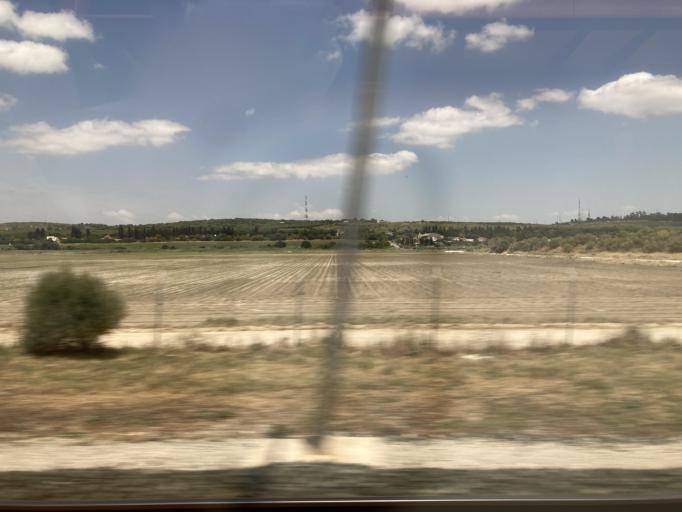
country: ES
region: Andalusia
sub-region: Provincia de Cadiz
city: El Puerto de Santa Maria
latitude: 36.6190
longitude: -6.1700
